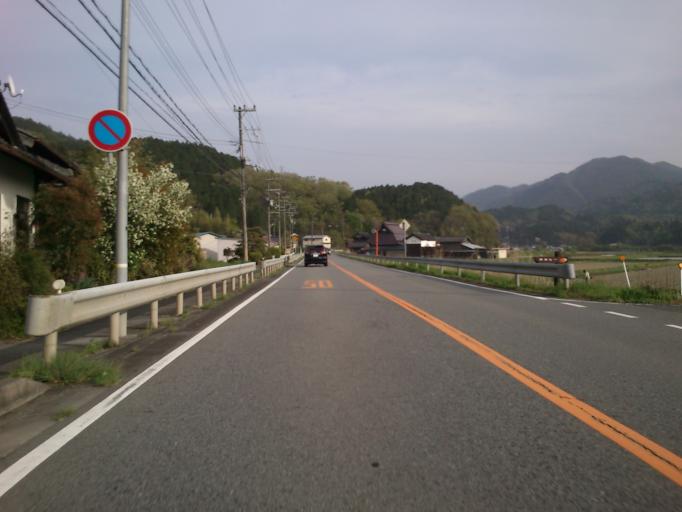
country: JP
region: Hyogo
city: Sasayama
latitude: 35.0885
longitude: 135.3171
